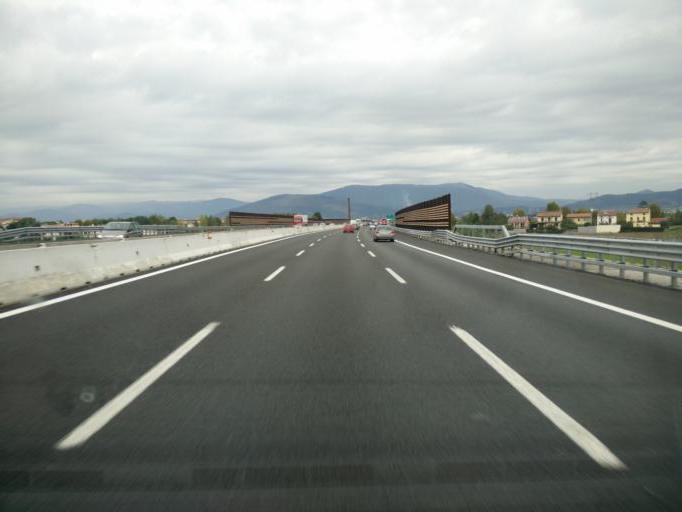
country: IT
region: Tuscany
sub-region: Province of Florence
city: San Donnino
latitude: 43.8127
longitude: 11.1517
